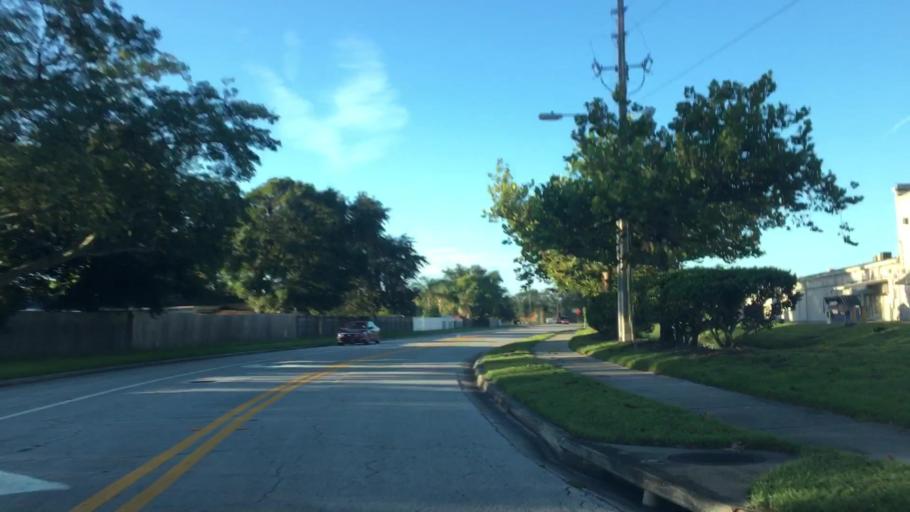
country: US
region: Florida
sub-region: Orange County
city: Conway
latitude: 28.4834
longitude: -81.3069
